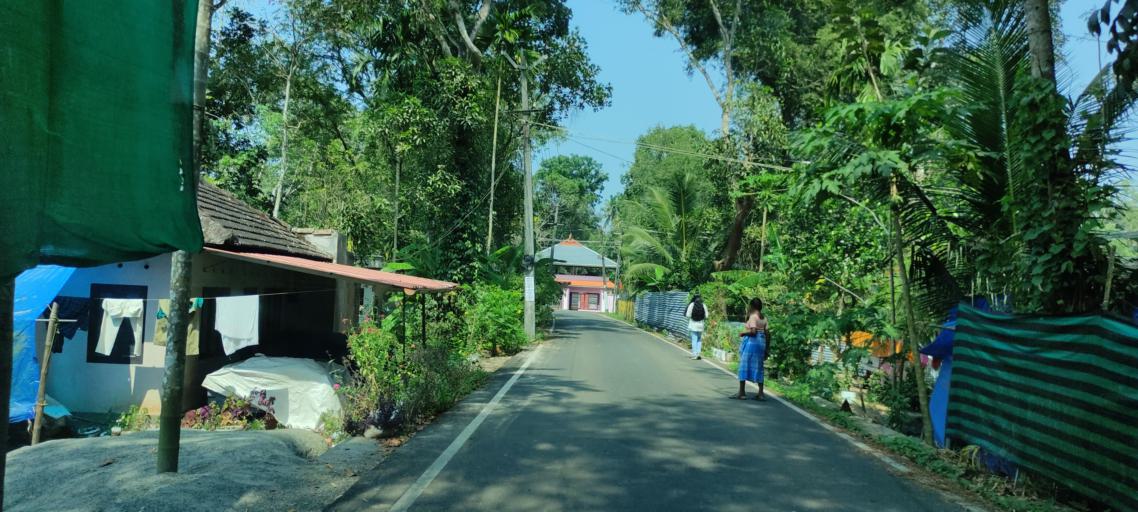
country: IN
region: Kerala
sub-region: Alappuzha
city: Alleppey
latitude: 9.5515
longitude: 76.3197
